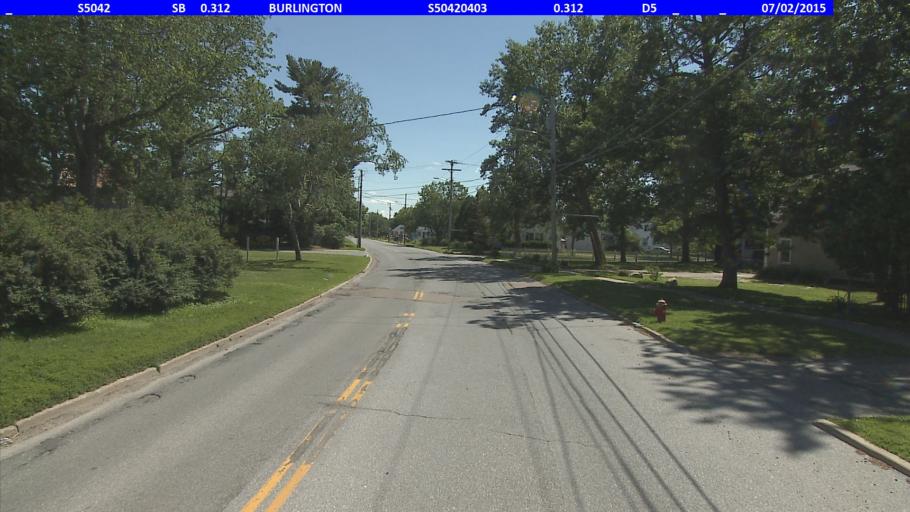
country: US
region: Vermont
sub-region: Chittenden County
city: Burlington
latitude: 44.5203
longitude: -73.2574
